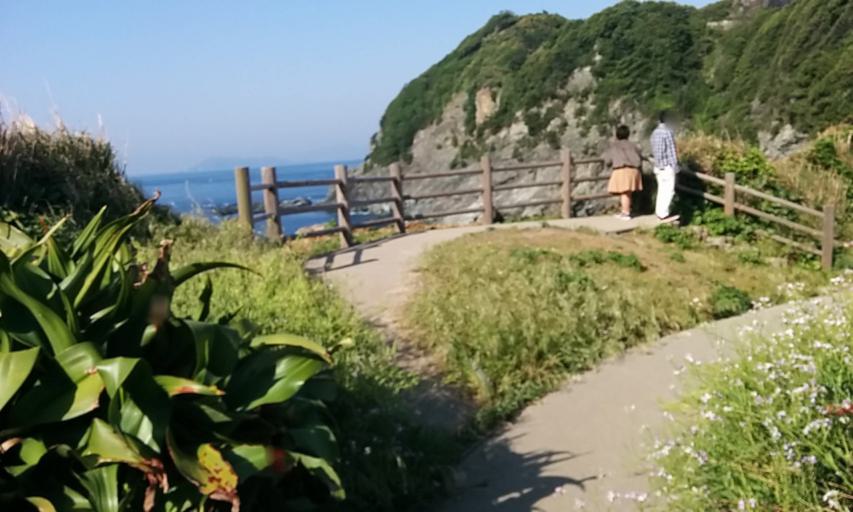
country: JP
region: Oita
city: Tsukumiura
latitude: 33.3451
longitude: 132.0189
